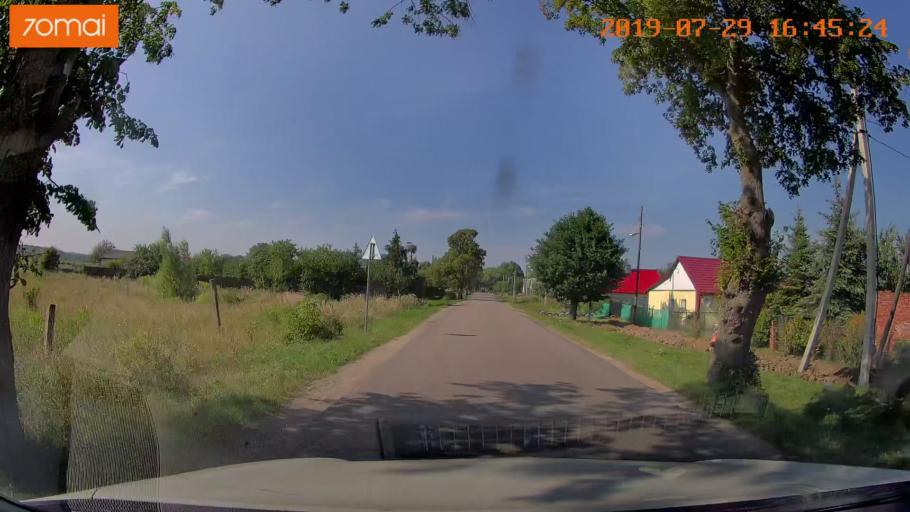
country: RU
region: Kaliningrad
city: Primorsk
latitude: 54.7645
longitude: 20.0808
